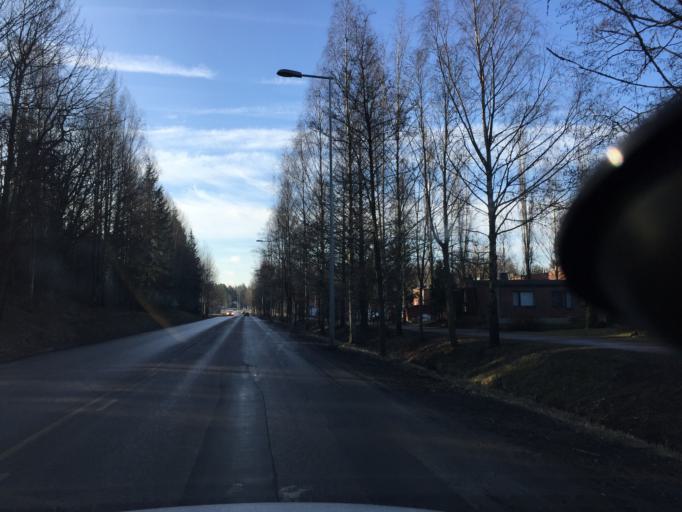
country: FI
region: Uusimaa
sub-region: Helsinki
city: Teekkarikylae
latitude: 60.2820
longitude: 24.8726
